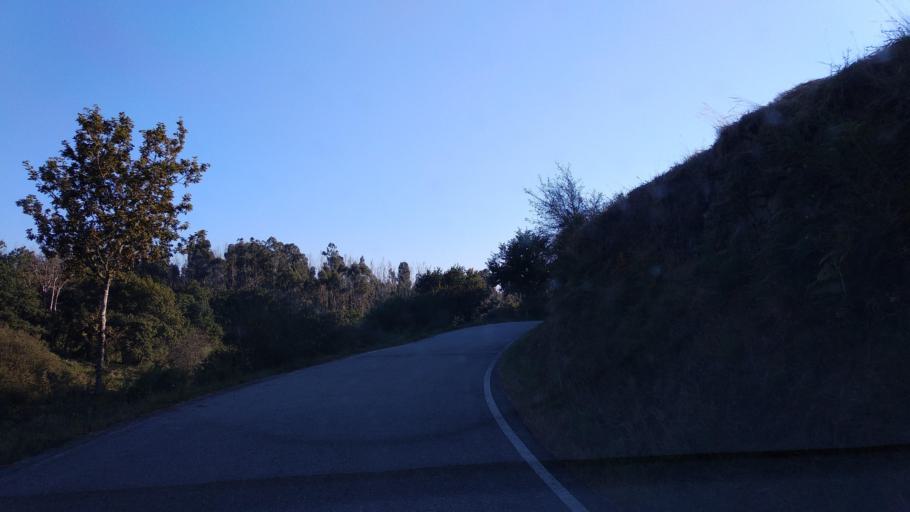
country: ES
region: Galicia
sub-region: Provincia de Pontevedra
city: Ponte Caldelas
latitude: 42.3579
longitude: -8.4935
